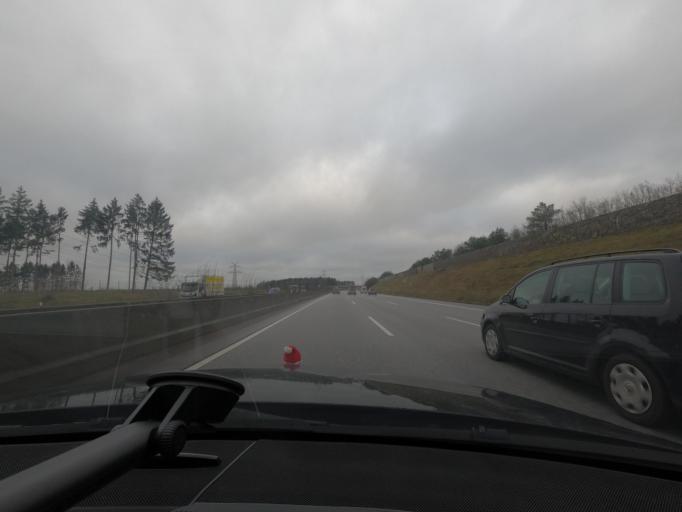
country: DE
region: Schleswig-Holstein
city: Kaltenkirchen
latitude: 53.8302
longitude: 9.9242
